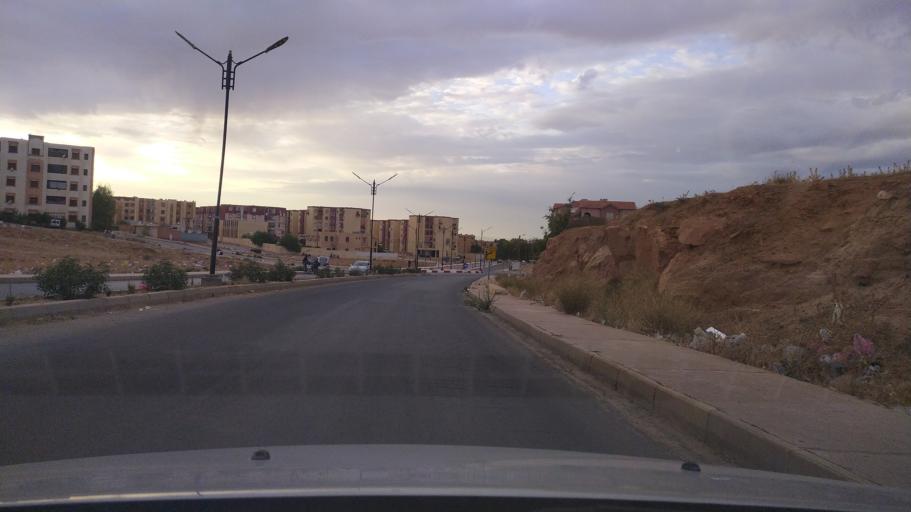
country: DZ
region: Tiaret
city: Frenda
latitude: 35.0532
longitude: 1.0634
